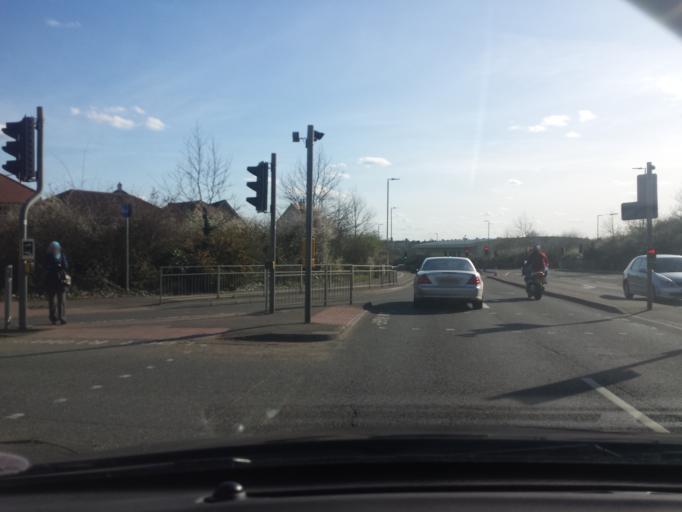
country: GB
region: England
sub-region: Essex
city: Colchester
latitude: 51.9032
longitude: 0.8979
